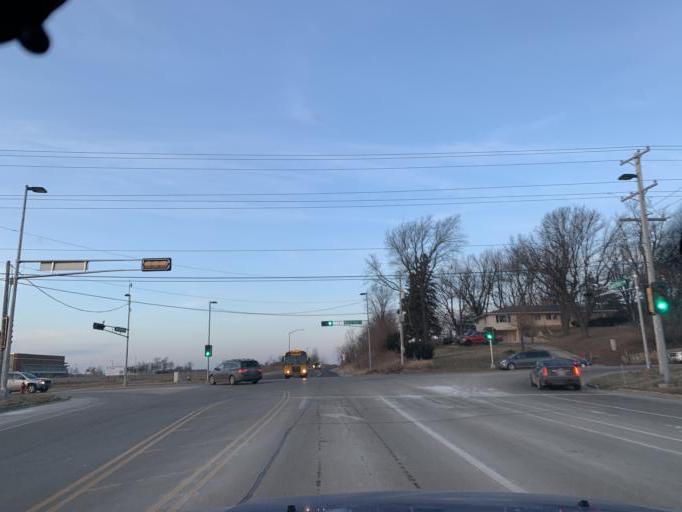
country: US
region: Wisconsin
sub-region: Dane County
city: Middleton
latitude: 43.0598
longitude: -89.5521
